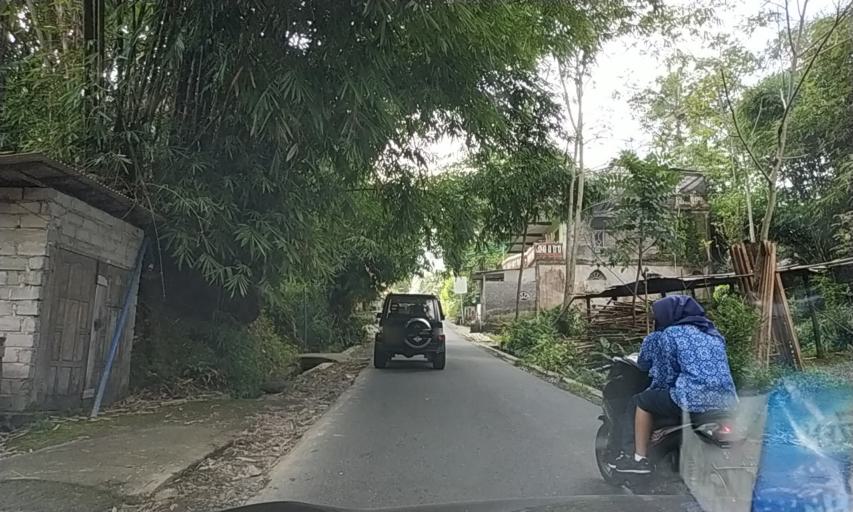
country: ID
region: Central Java
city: Jogonalan
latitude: -7.6287
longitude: 110.4685
